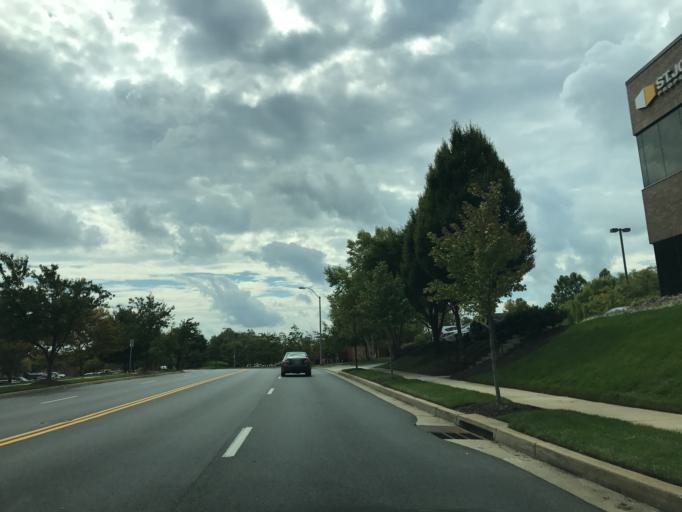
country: US
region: Maryland
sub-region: Baltimore County
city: Woodlawn
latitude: 39.3261
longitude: -76.7509
